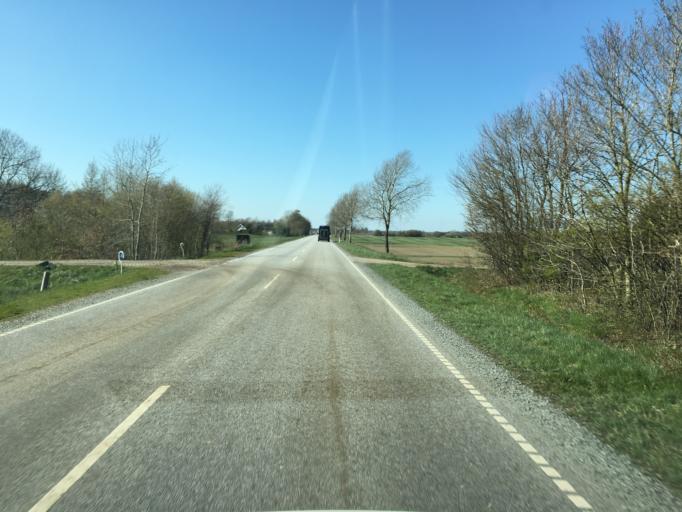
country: DK
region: South Denmark
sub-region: Aabenraa Kommune
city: Tinglev
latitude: 54.9569
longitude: 9.3347
